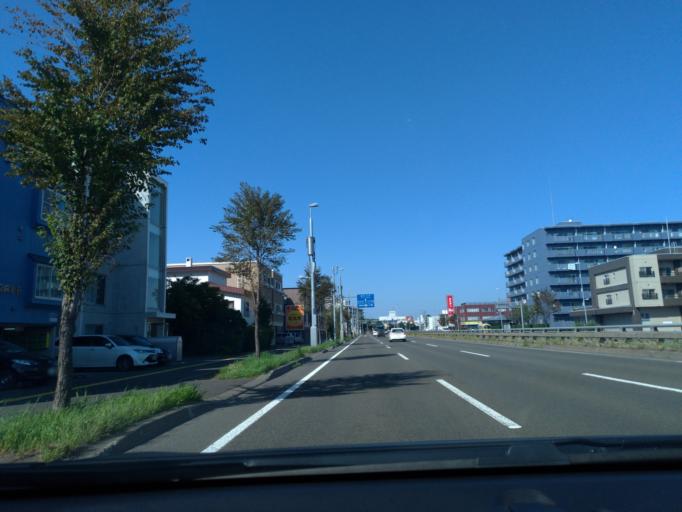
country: JP
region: Hokkaido
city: Sapporo
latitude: 43.1077
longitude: 141.3439
